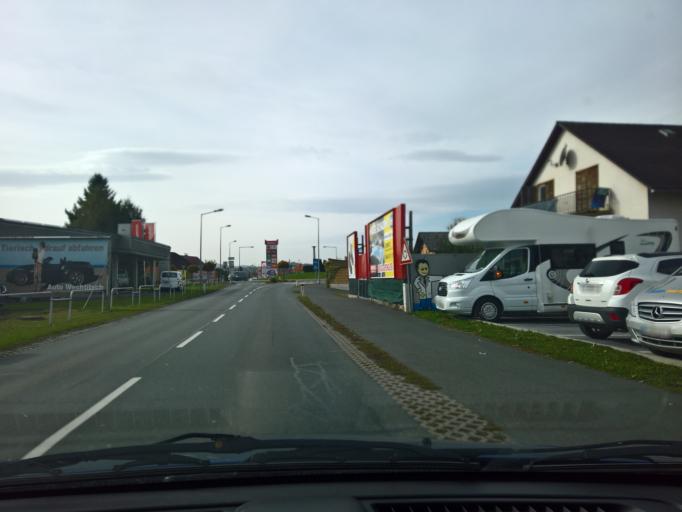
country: AT
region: Styria
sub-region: Politischer Bezirk Leibnitz
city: Kaindorf an der Sulm
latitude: 46.7981
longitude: 15.5591
